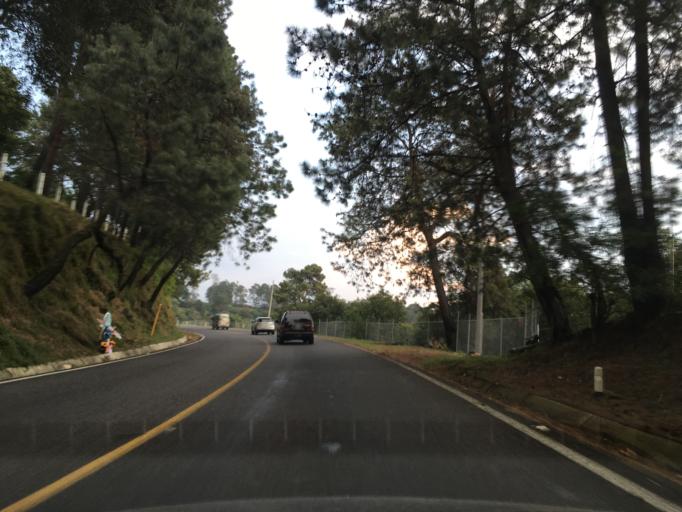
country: MX
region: Michoacan
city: Tingambato
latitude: 19.4749
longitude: -101.9128
